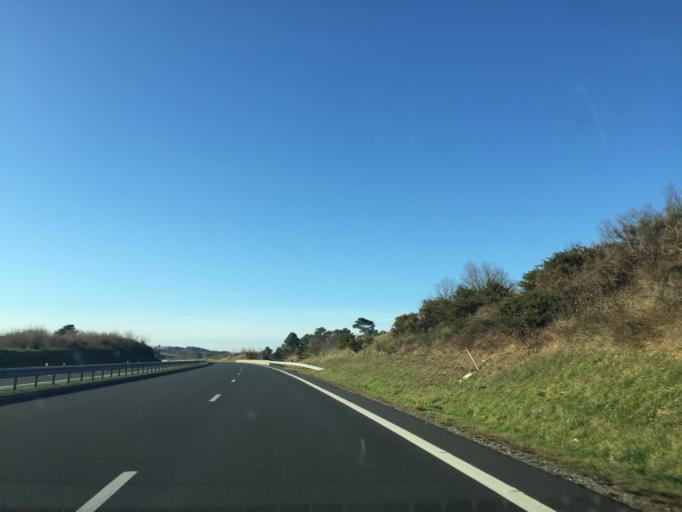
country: FR
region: Limousin
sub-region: Departement de la Correze
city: Cublac
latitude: 45.1731
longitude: 1.3168
